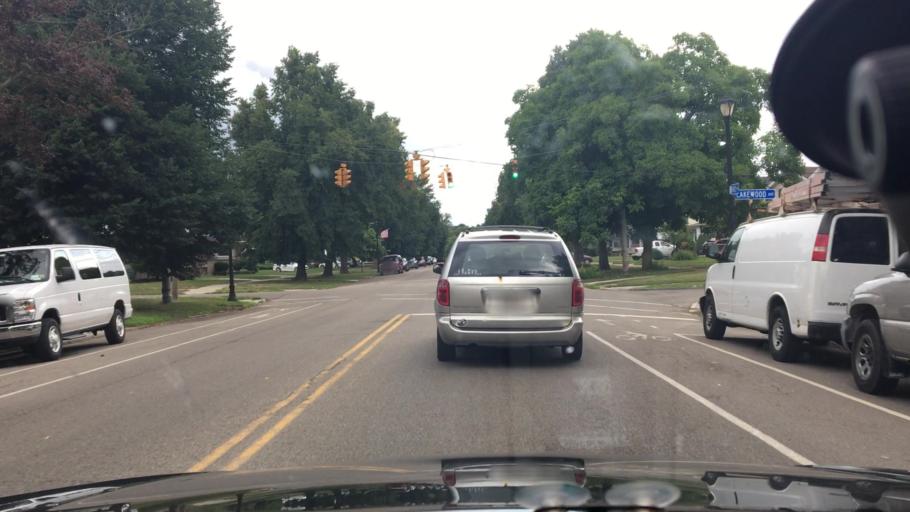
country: US
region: New York
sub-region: Erie County
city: West Seneca
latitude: 42.8526
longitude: -78.8213
